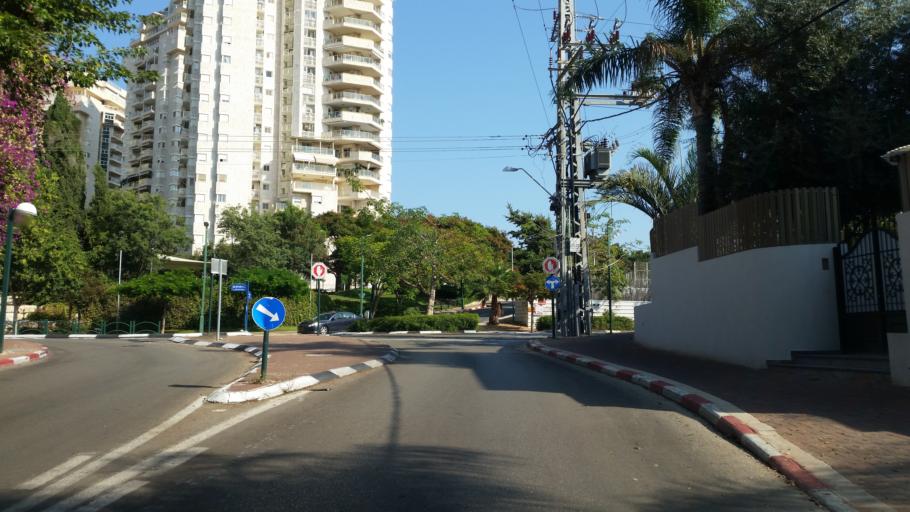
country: IL
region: Tel Aviv
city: Ramat HaSharon
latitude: 32.1495
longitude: 34.8465
